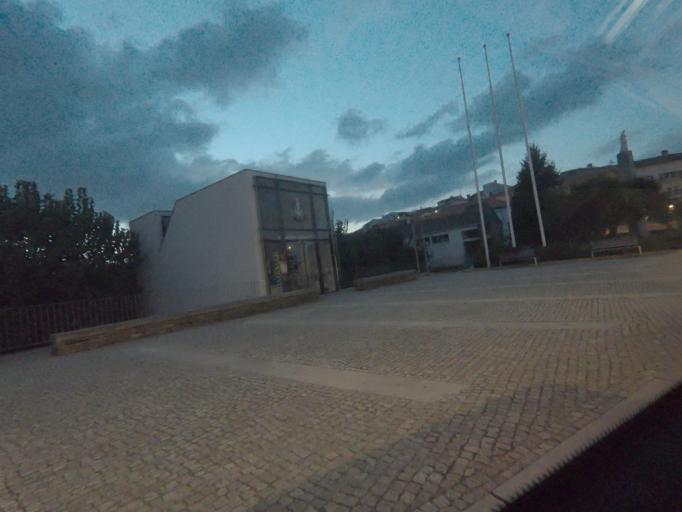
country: PT
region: Vila Real
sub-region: Mesao Frio
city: Mesao Frio
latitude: 41.1403
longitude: -7.8981
